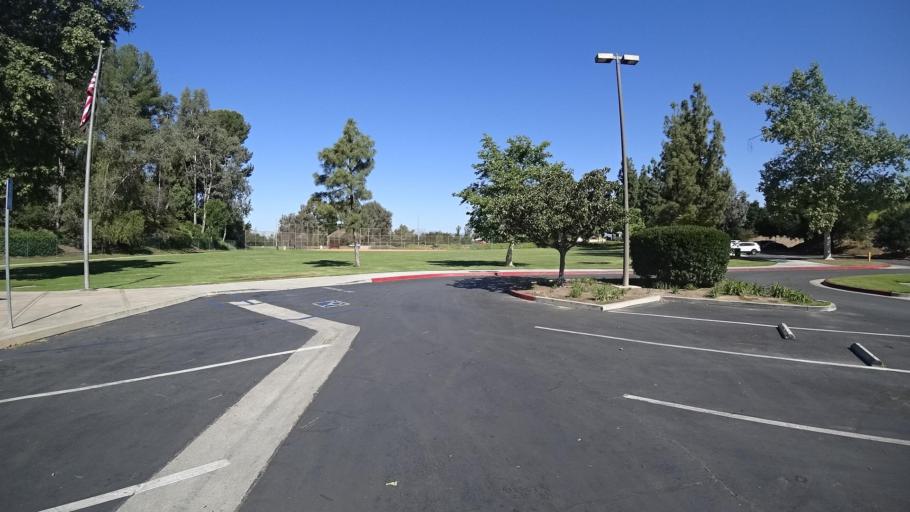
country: US
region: California
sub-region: Los Angeles County
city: Diamond Bar
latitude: 34.0095
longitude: -117.8145
